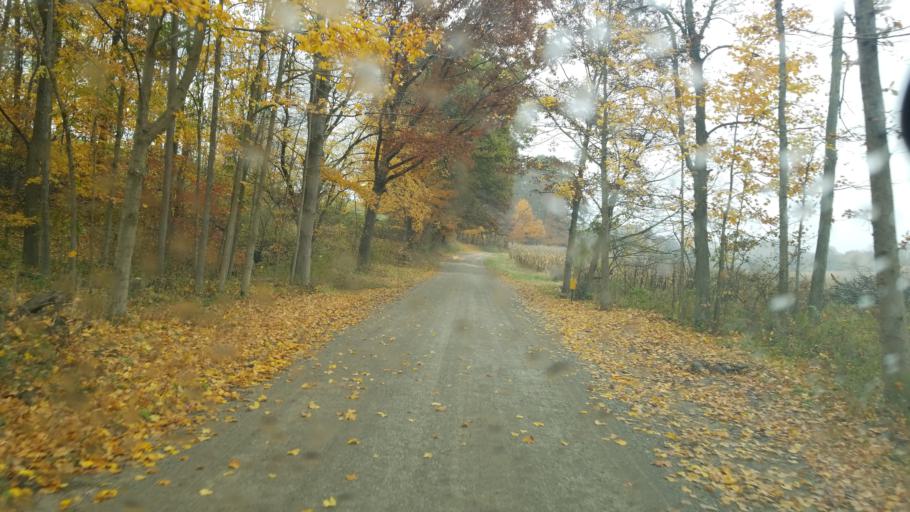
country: US
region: Ohio
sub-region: Holmes County
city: Millersburg
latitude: 40.4551
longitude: -81.8527
